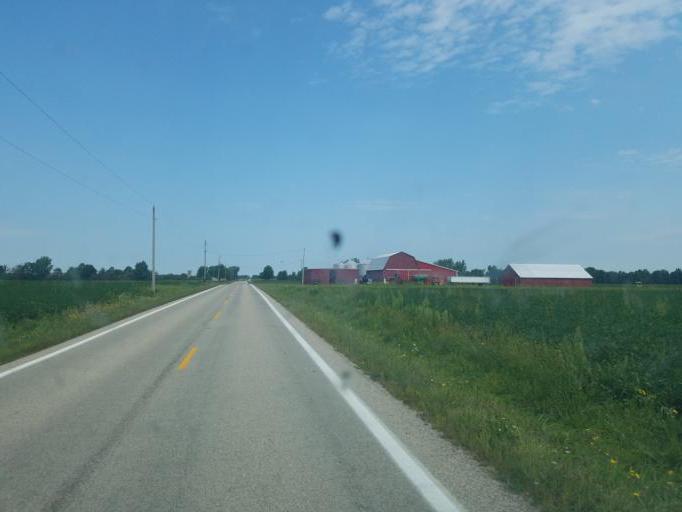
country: US
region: Ohio
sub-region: Marion County
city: Marion
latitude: 40.5897
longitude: -83.2174
